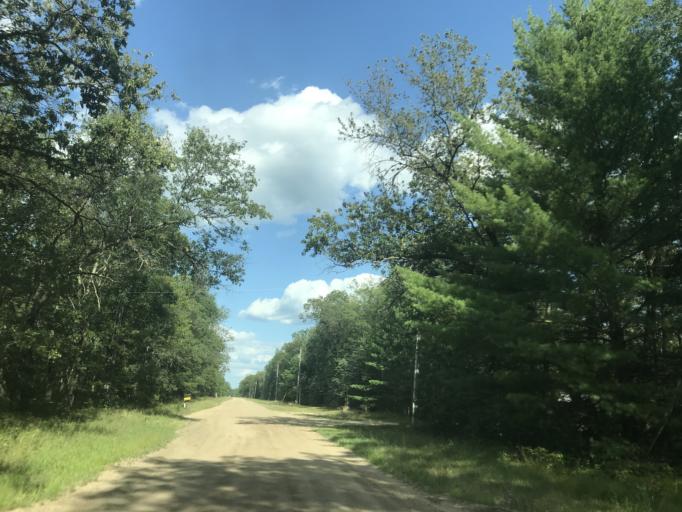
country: US
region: Michigan
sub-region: Newaygo County
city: Newaygo
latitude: 43.4492
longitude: -85.7582
